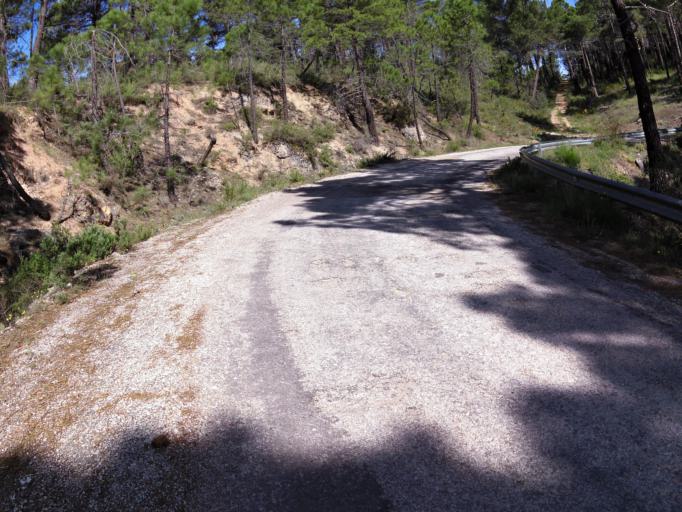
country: ES
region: Castille-La Mancha
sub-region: Provincia de Albacete
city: Riopar
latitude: 38.5236
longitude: -2.4373
